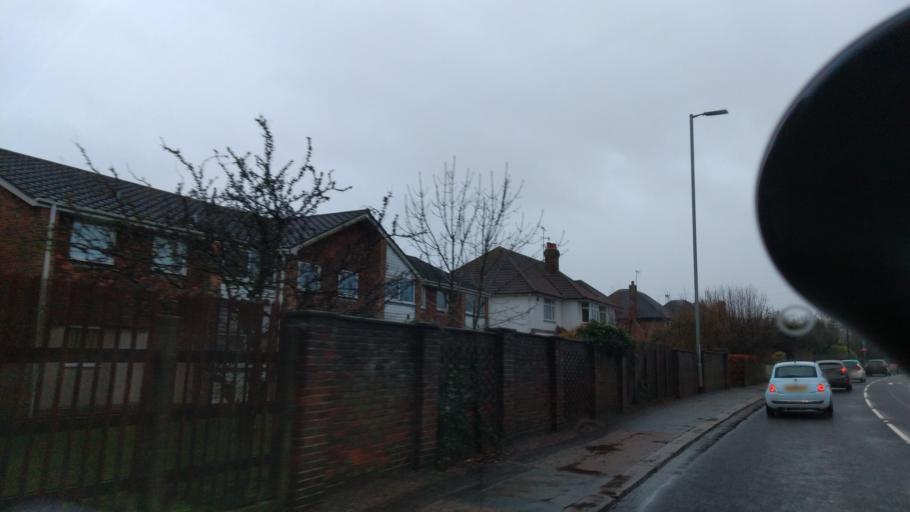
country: GB
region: England
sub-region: West Sussex
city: Broadwater
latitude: 50.8334
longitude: -0.3746
